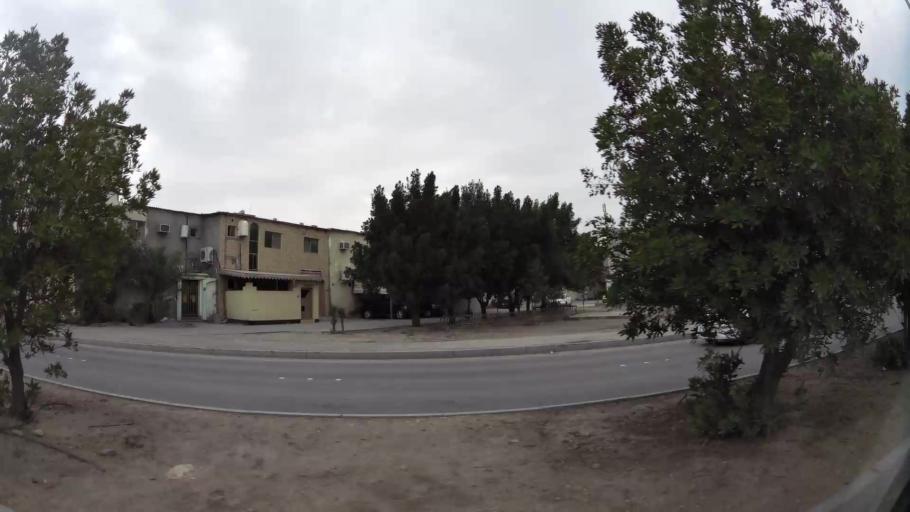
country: BH
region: Northern
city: Sitrah
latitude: 26.1644
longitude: 50.6153
